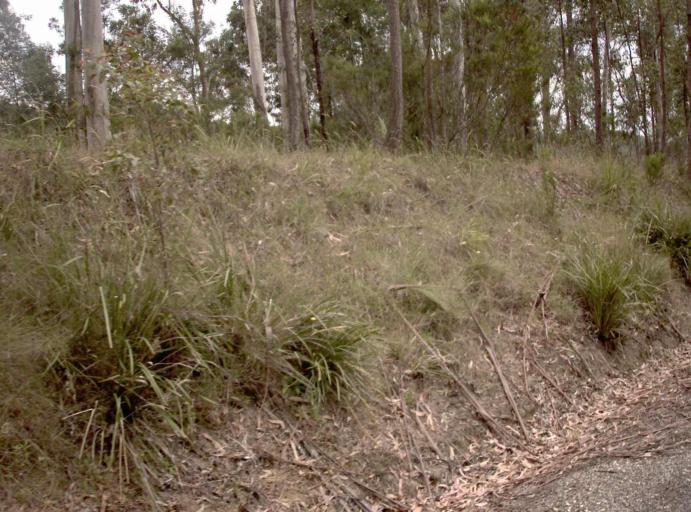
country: AU
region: New South Wales
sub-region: Bombala
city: Bombala
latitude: -37.4423
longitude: 149.1952
